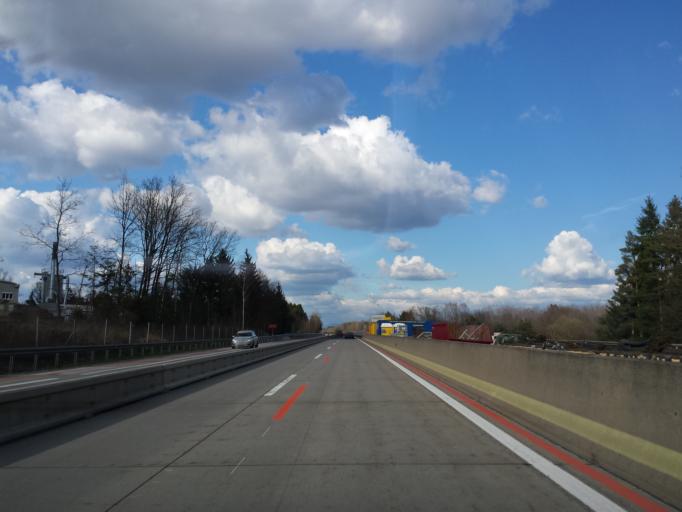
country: AT
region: Styria
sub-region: Politischer Bezirk Graz-Umgebung
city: Unterpremstatten
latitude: 46.9645
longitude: 15.3842
